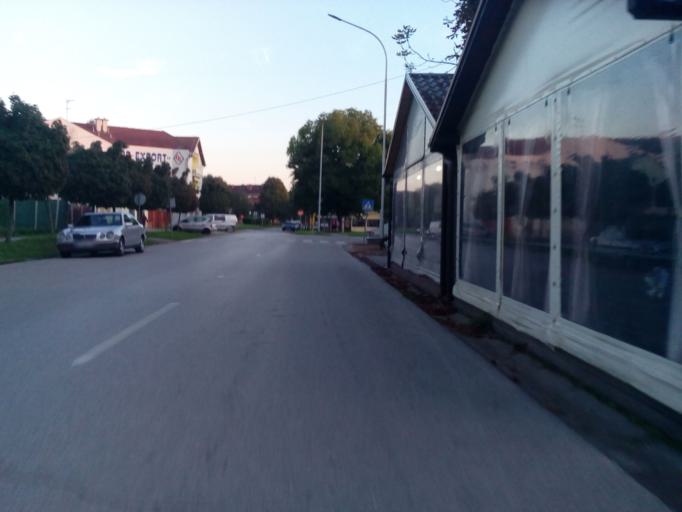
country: HR
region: Vukovarsko-Srijemska
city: Vinkovci
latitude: 45.2973
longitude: 18.8041
